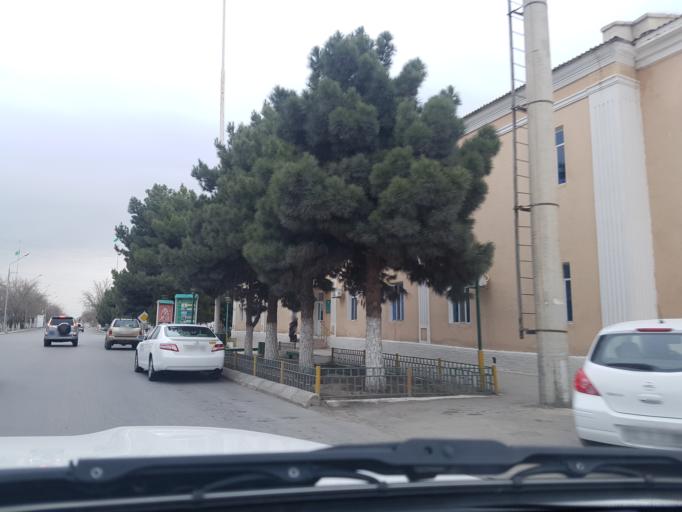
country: TM
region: Balkan
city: Balkanabat
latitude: 39.5039
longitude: 54.3634
